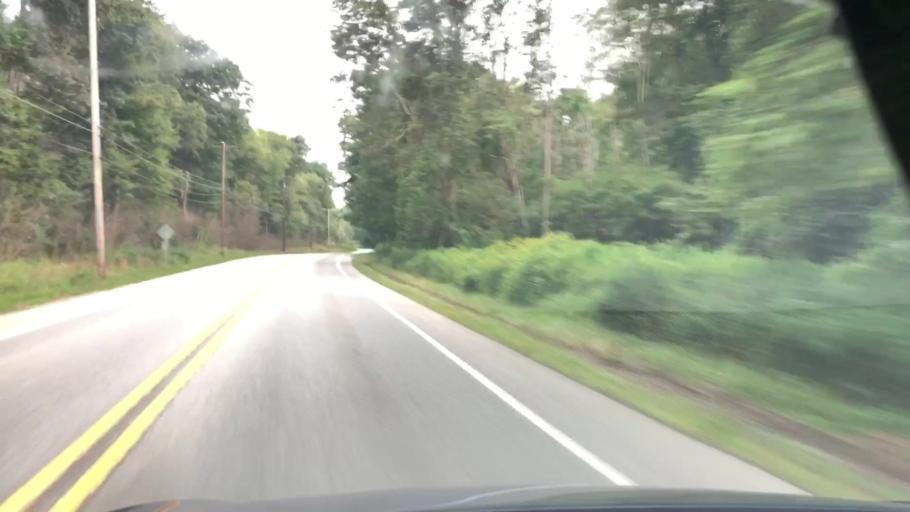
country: US
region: Pennsylvania
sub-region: Venango County
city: Hasson Heights
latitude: 41.4871
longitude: -79.6988
